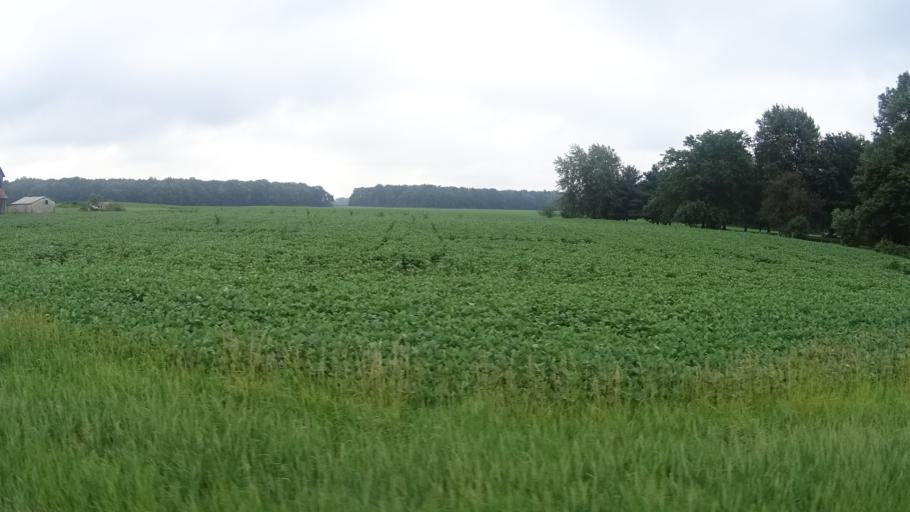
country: US
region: Ohio
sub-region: Erie County
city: Milan
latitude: 41.2939
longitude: -82.5290
